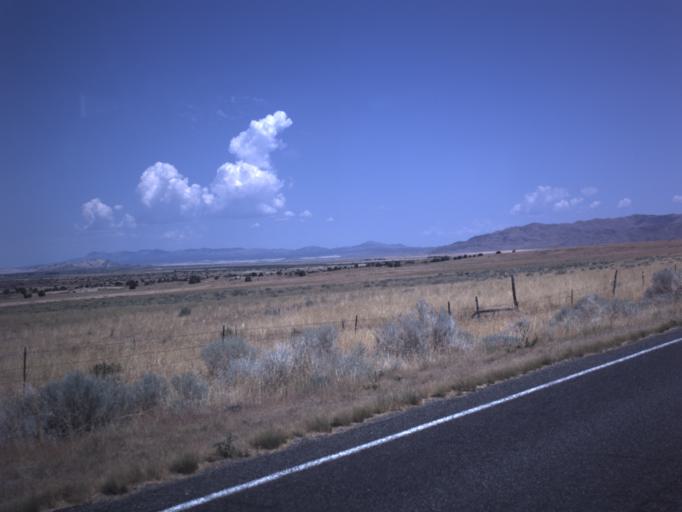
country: US
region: Utah
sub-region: Millard County
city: Delta
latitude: 39.4405
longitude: -112.3158
